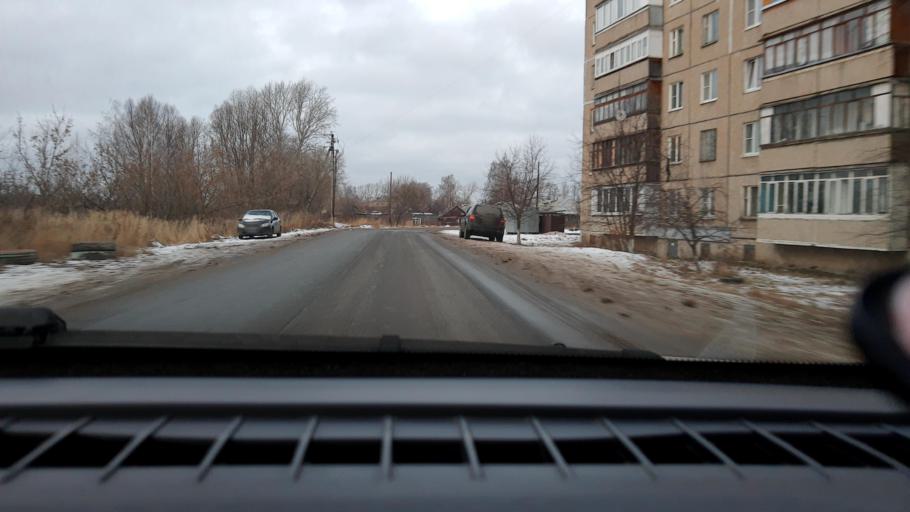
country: RU
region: Nizjnij Novgorod
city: Gorbatovka
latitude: 56.2447
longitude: 43.7454
